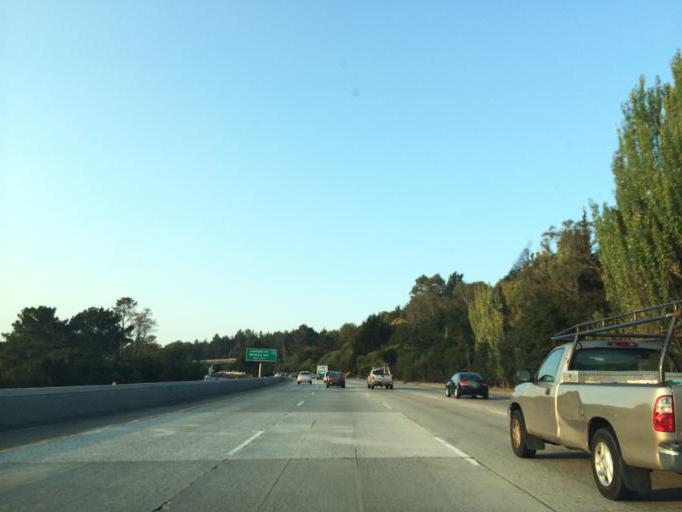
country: US
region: California
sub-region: San Mateo County
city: San Bruno
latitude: 37.6102
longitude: -122.4273
